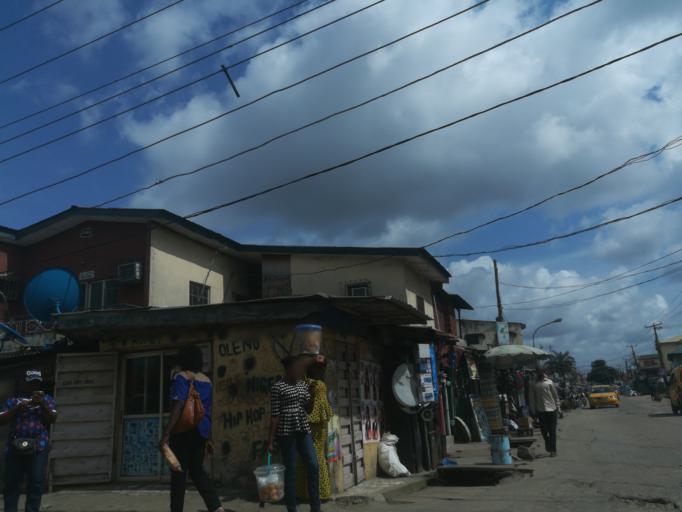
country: NG
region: Lagos
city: Somolu
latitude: 6.5304
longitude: 3.3804
